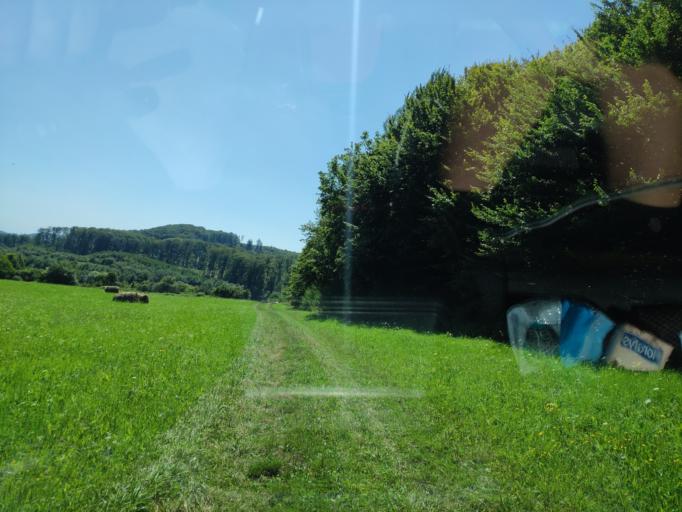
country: SK
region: Kosicky
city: Secovce
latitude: 48.6346
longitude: 21.4573
